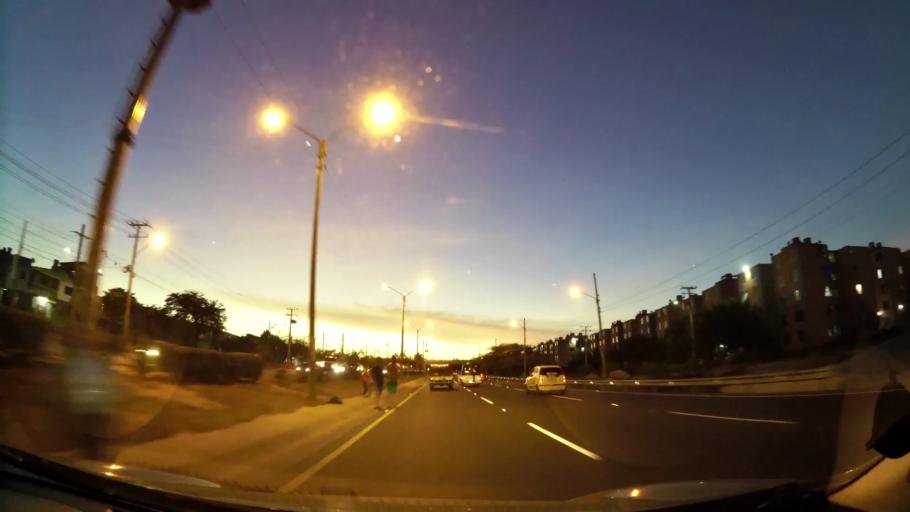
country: CO
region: Atlantico
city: Soledad
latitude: 10.9229
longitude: -74.8093
